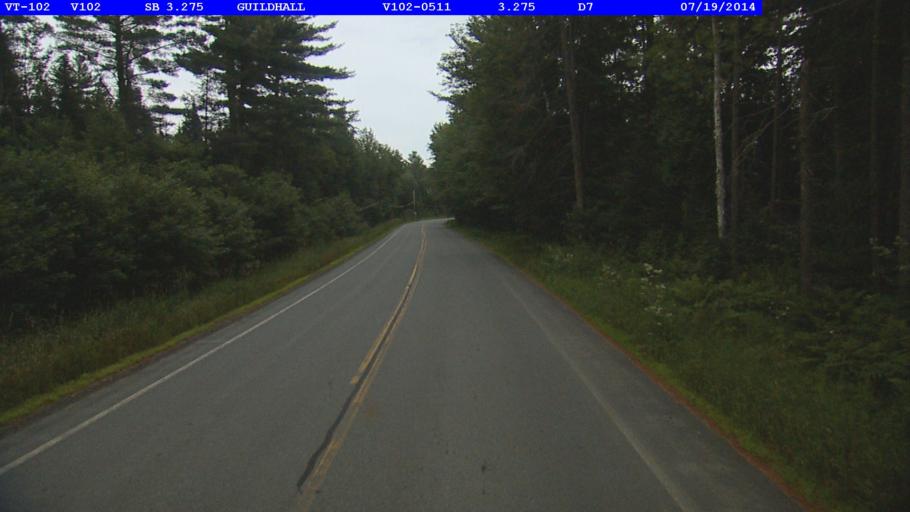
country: US
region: New Hampshire
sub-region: Coos County
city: Northumberland
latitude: 44.5402
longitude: -71.5840
